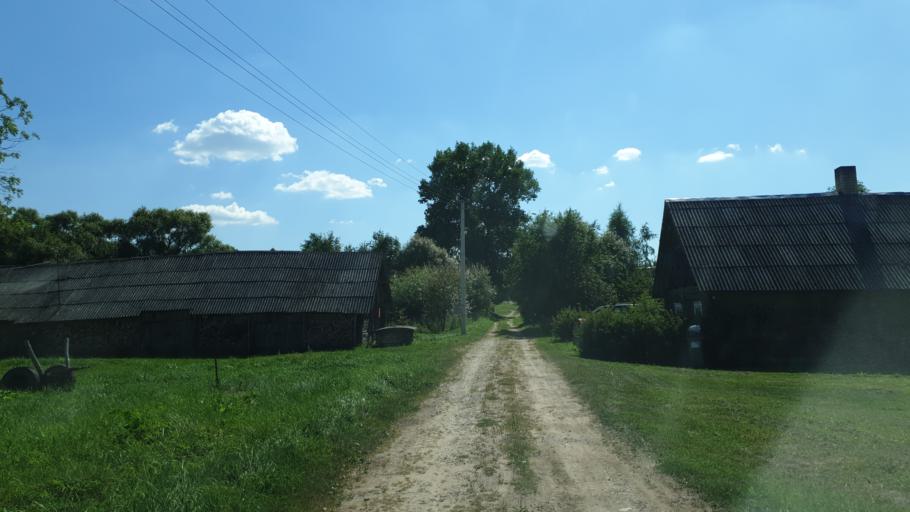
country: LT
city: Sirvintos
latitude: 54.9028
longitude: 24.9112
